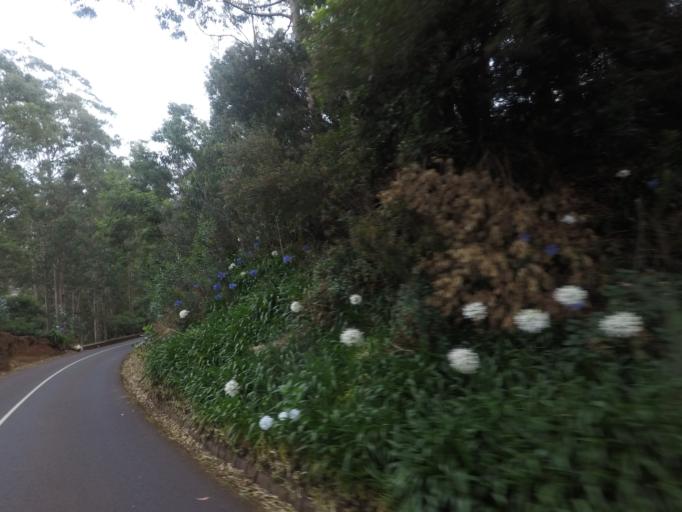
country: PT
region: Madeira
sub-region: Funchal
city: Nossa Senhora do Monte
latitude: 32.6685
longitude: -16.8792
